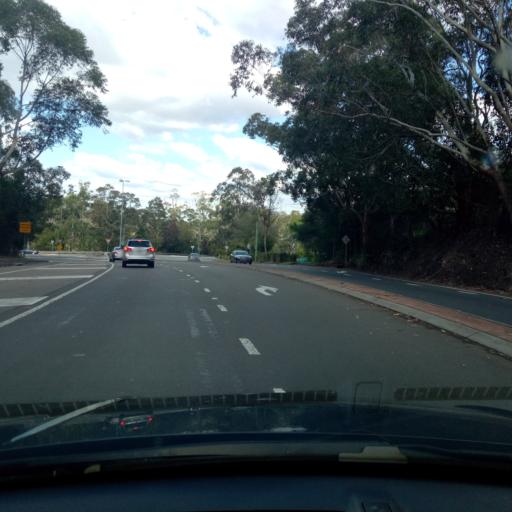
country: AU
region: New South Wales
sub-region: Gosford Shire
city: Narara
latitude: -33.3969
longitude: 151.3448
